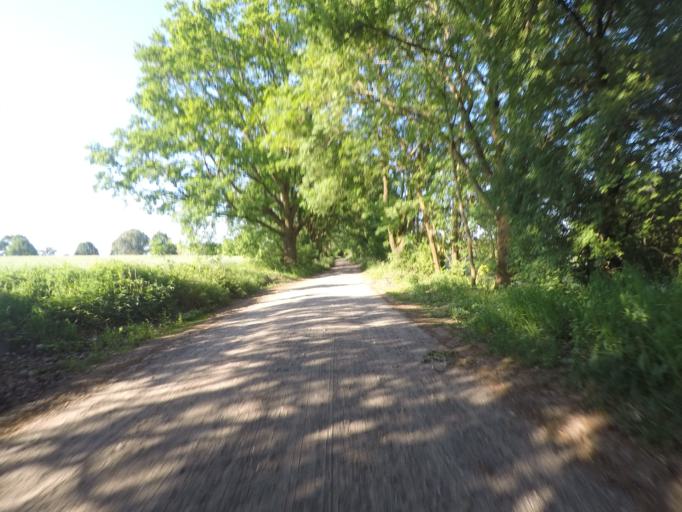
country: DE
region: Brandenburg
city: Joachimsthal
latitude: 52.8863
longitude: 13.6962
